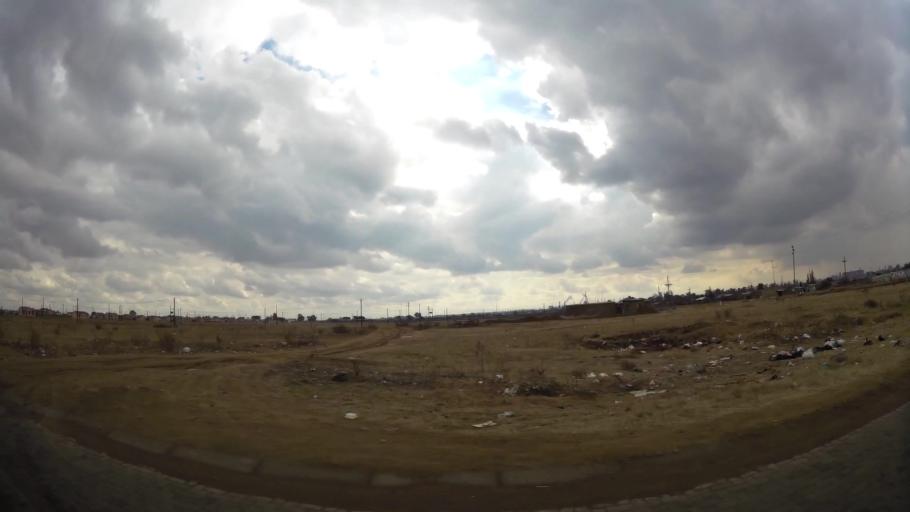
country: ZA
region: Orange Free State
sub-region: Fezile Dabi District Municipality
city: Sasolburg
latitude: -26.8583
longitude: 27.8726
